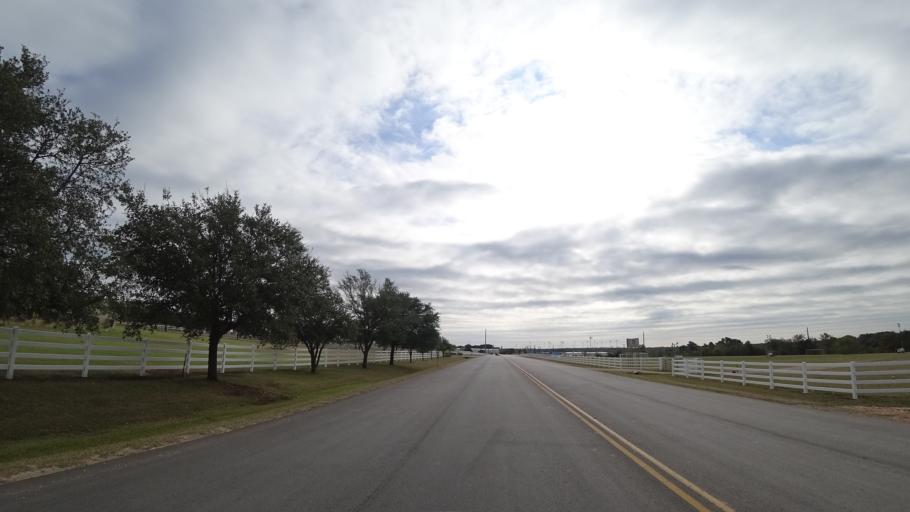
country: US
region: Texas
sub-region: Travis County
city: Manchaca
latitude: 30.1367
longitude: -97.8560
